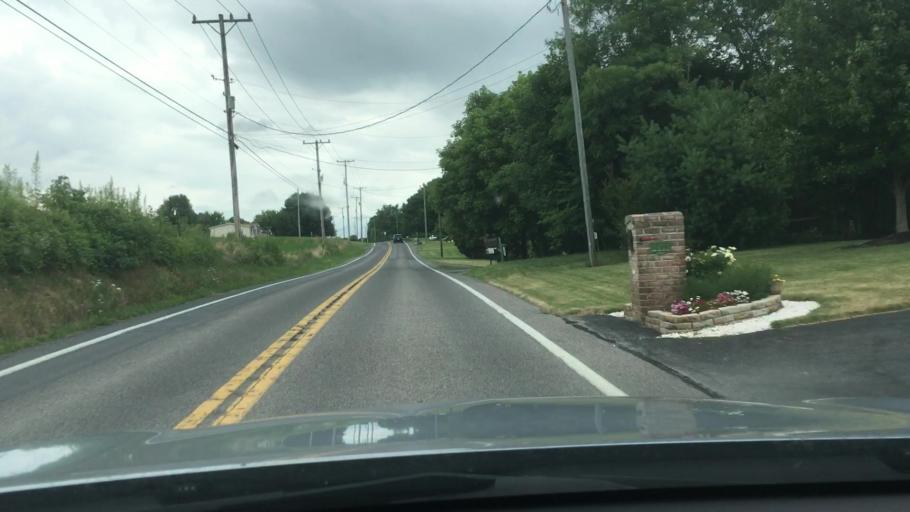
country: US
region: Pennsylvania
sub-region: Franklin County
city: Greencastle
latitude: 39.8784
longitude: -77.7282
